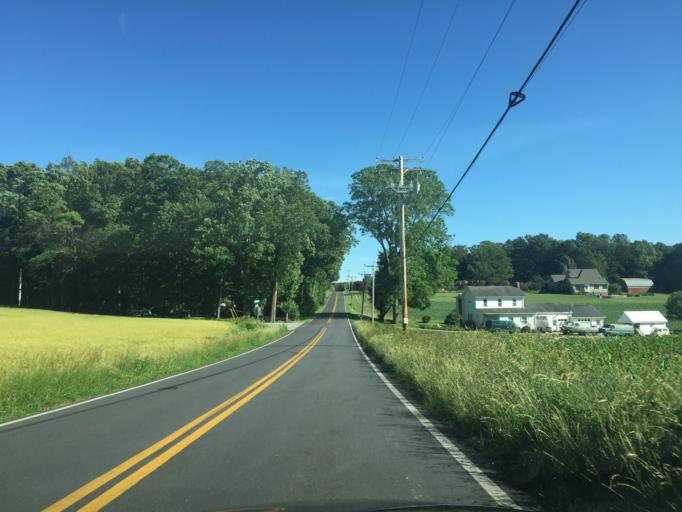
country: US
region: Maryland
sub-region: Carroll County
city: Westminster
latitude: 39.5897
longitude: -76.9315
